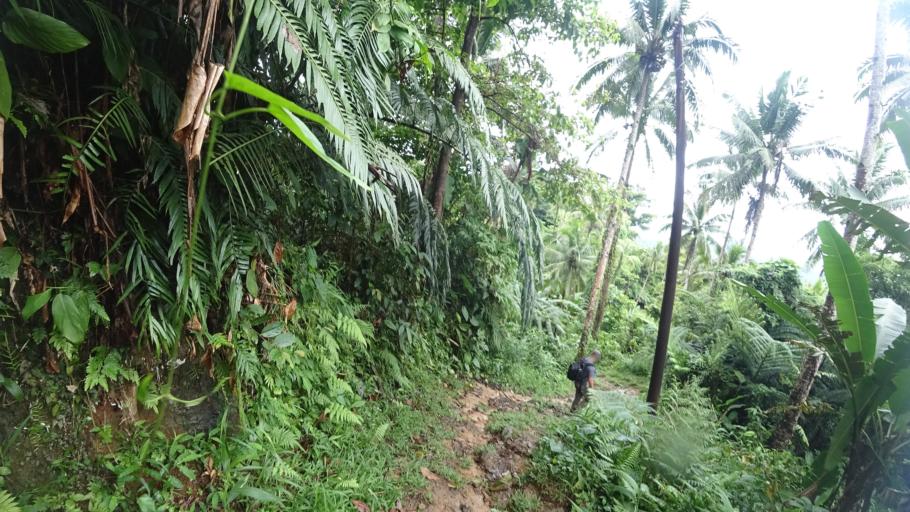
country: PH
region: Eastern Visayas
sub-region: Province of Leyte
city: Bugho
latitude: 10.8273
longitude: 124.8735
